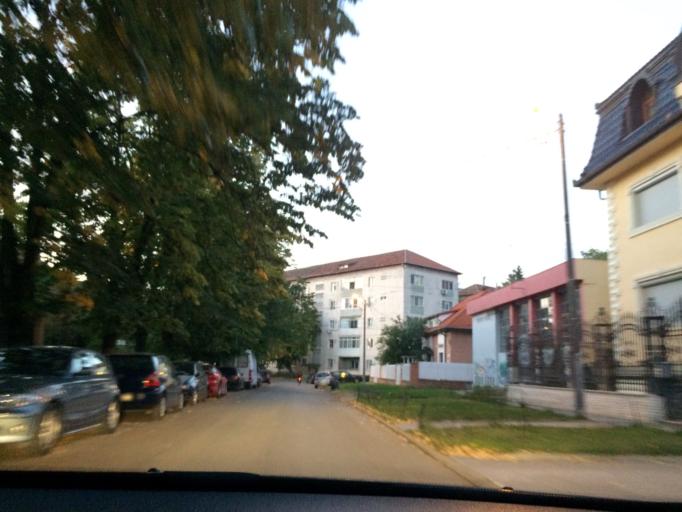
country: RO
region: Timis
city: Timisoara
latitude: 45.7600
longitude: 21.2127
